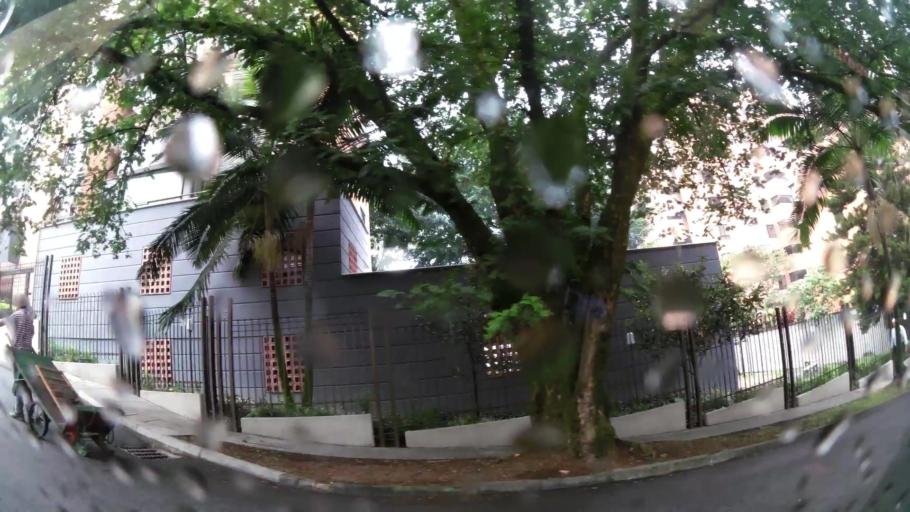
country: CO
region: Antioquia
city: Envigado
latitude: 6.2001
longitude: -75.5704
